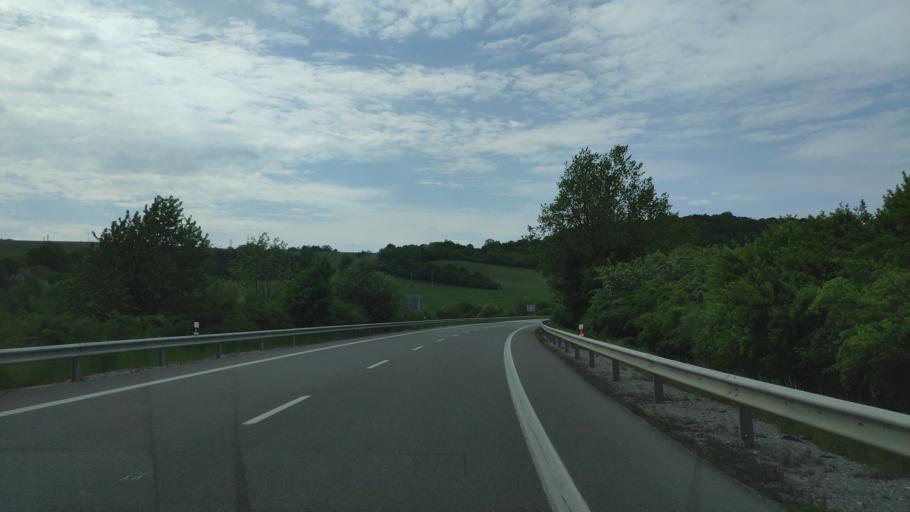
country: SK
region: Kosicky
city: Roznava
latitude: 48.5352
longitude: 20.3962
